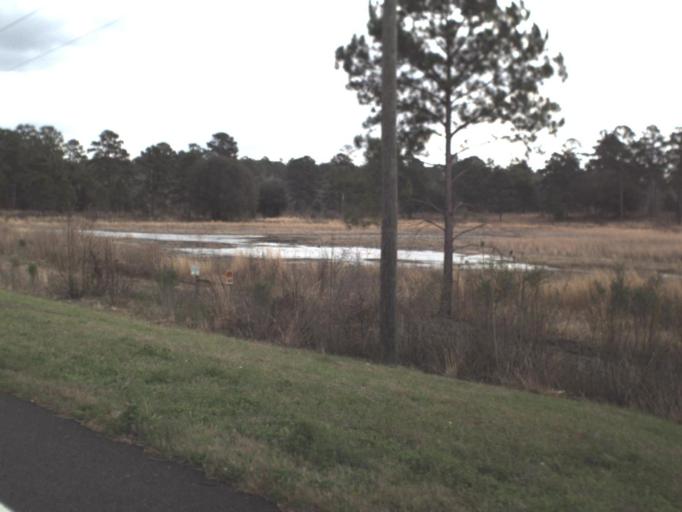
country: US
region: Florida
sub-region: Leon County
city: Tallahassee
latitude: 30.5980
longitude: -84.1855
